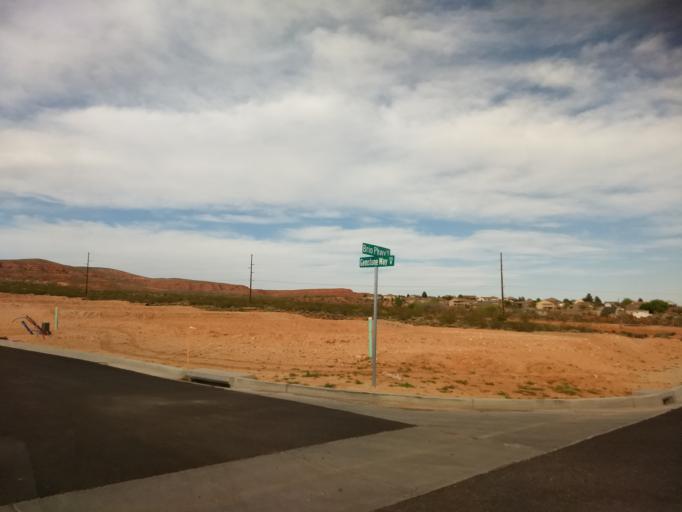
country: US
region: Utah
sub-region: Washington County
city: Washington
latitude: 37.1446
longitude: -113.5117
